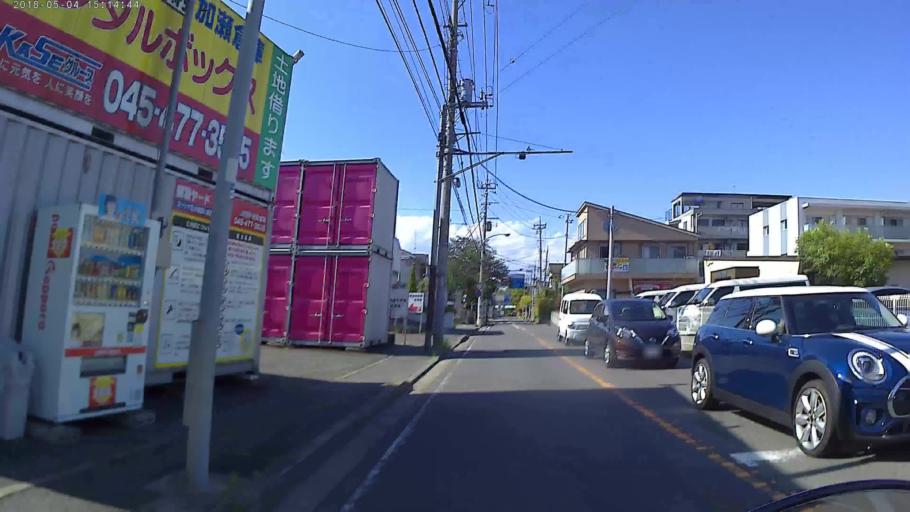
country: JP
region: Kanagawa
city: Yokohama
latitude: 35.5280
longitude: 139.6093
